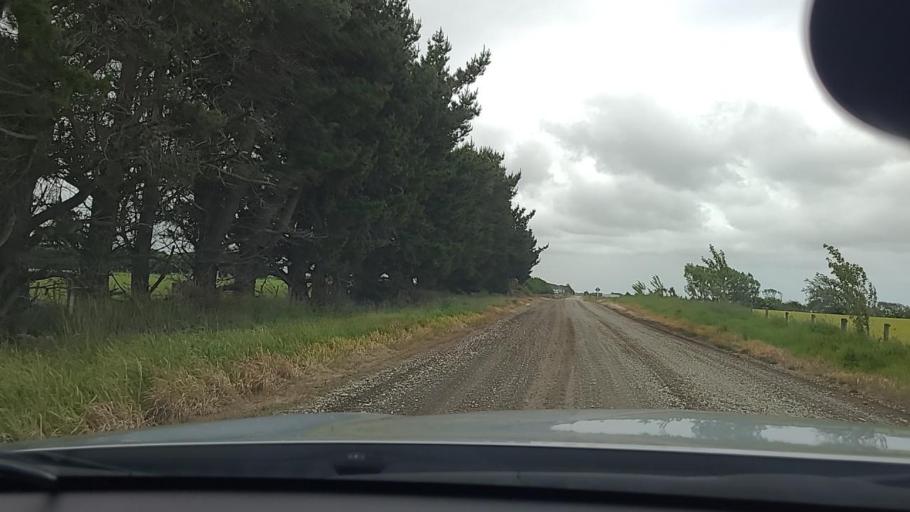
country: NZ
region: Southland
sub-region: Invercargill City
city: Invercargill
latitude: -46.3147
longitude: 168.2281
